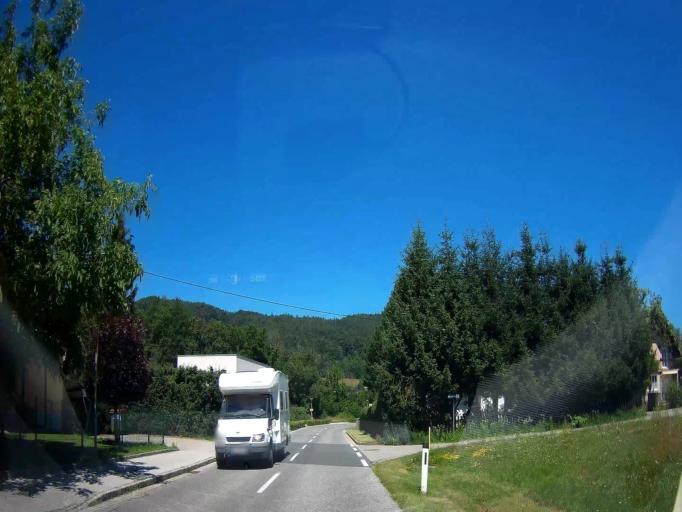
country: AT
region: Carinthia
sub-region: Politischer Bezirk Klagenfurt Land
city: Keutschach am See
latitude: 46.6002
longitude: 14.1739
